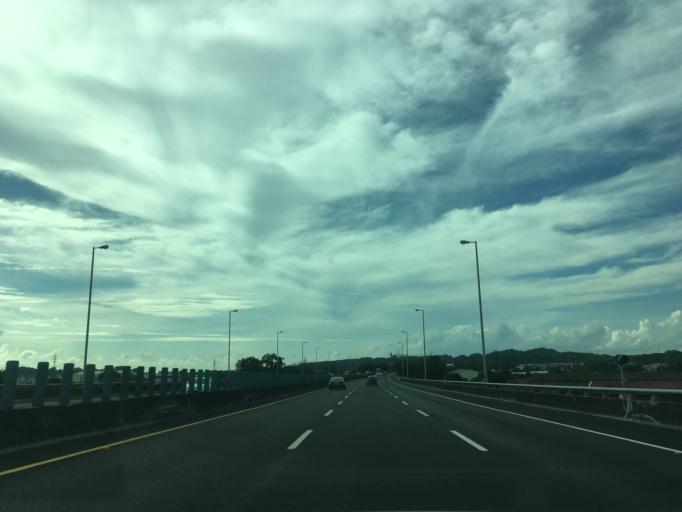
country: TW
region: Taiwan
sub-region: Chiayi
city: Jiayi Shi
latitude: 23.5058
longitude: 120.4898
